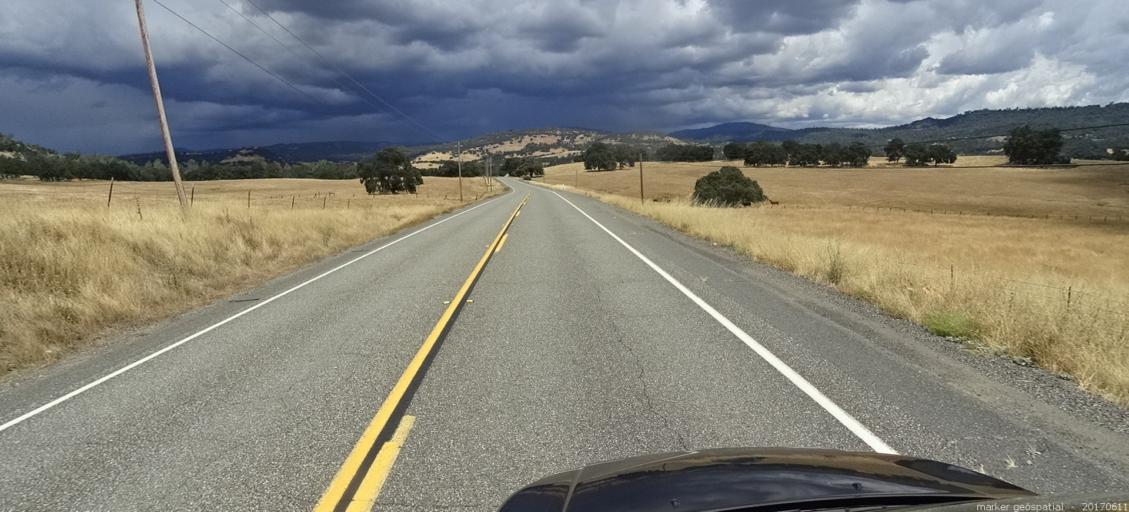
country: US
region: California
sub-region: Butte County
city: Paradise
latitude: 39.6509
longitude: -121.6001
